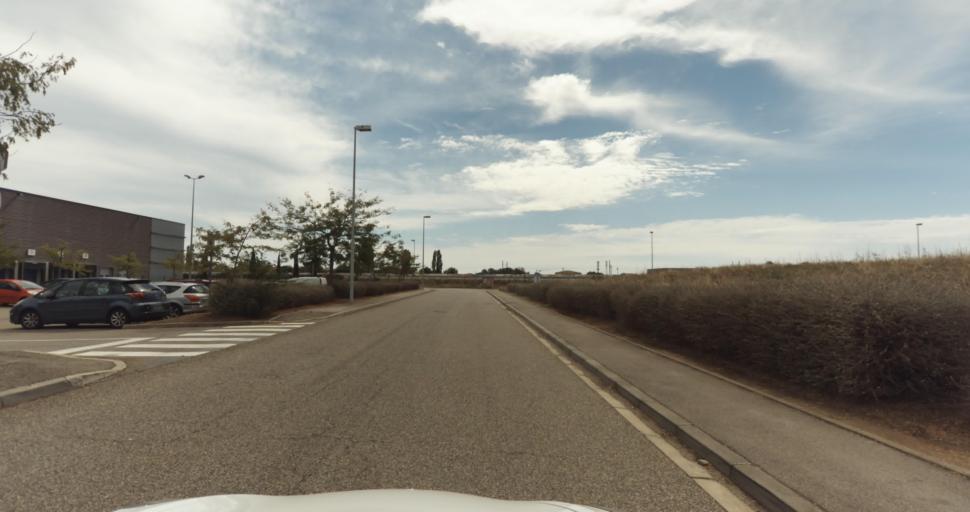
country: FR
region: Provence-Alpes-Cote d'Azur
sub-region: Departement des Bouches-du-Rhone
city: Miramas
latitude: 43.6015
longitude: 4.9951
